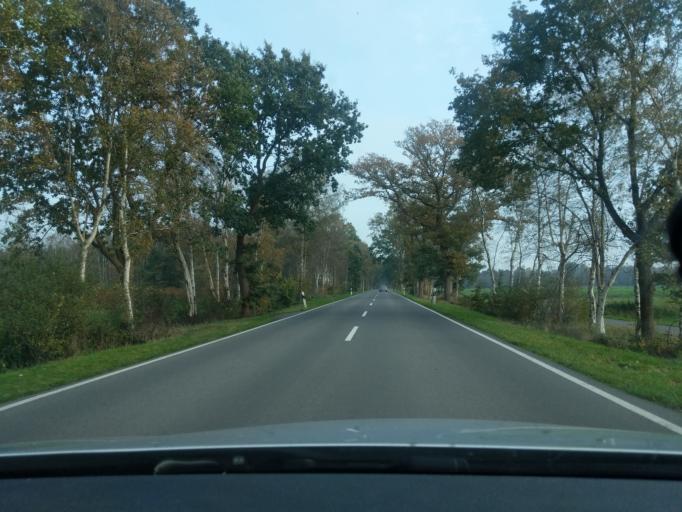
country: DE
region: Lower Saxony
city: Lamstedt
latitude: 53.6323
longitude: 9.1401
